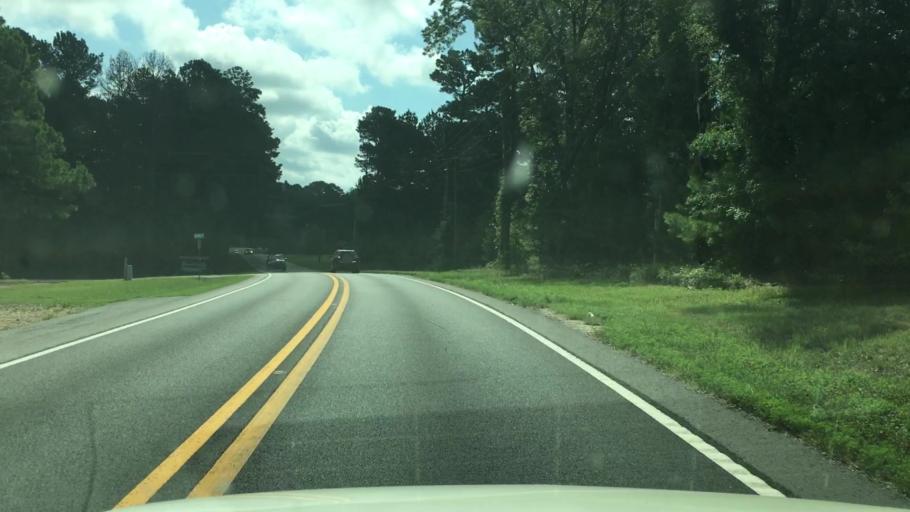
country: US
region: Arkansas
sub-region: Garland County
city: Lake Hamilton
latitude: 34.2789
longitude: -93.1572
